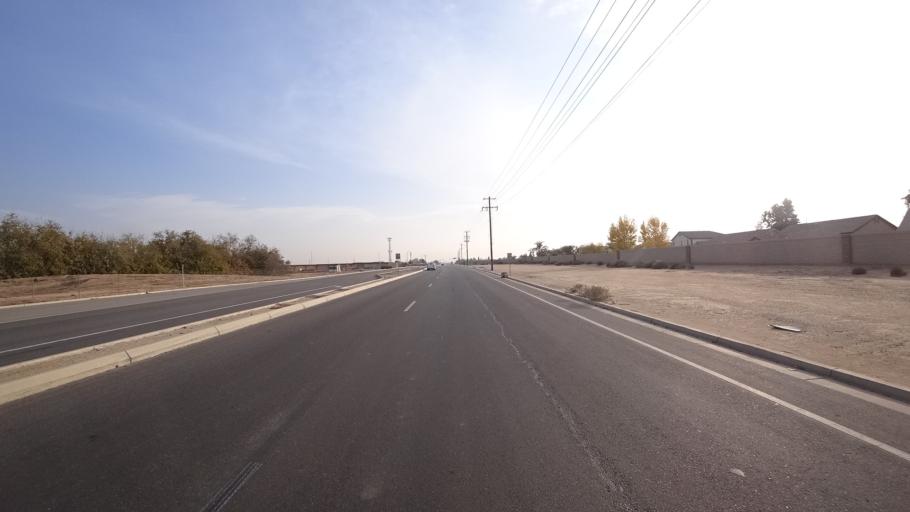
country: US
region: California
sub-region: Kern County
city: Greenacres
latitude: 35.4269
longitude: -119.1271
